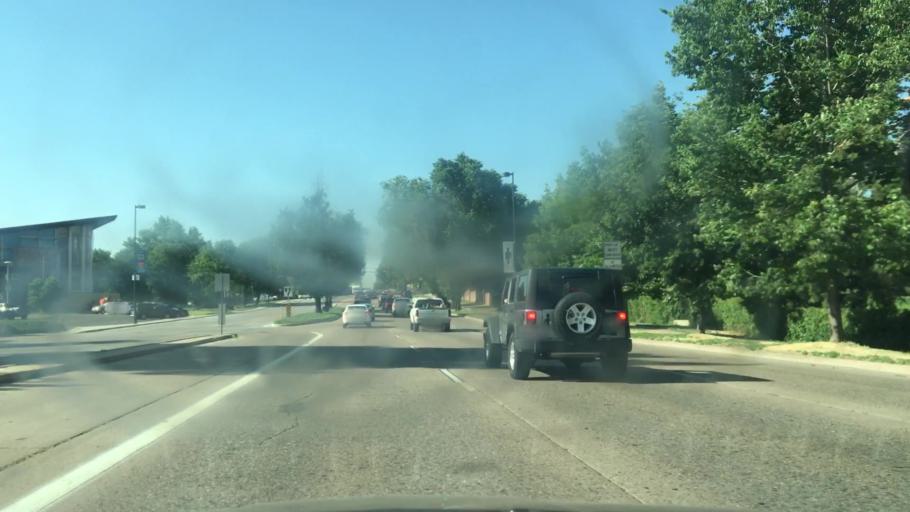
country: US
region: Colorado
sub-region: Arapahoe County
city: Glendale
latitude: 39.7134
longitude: -104.9593
